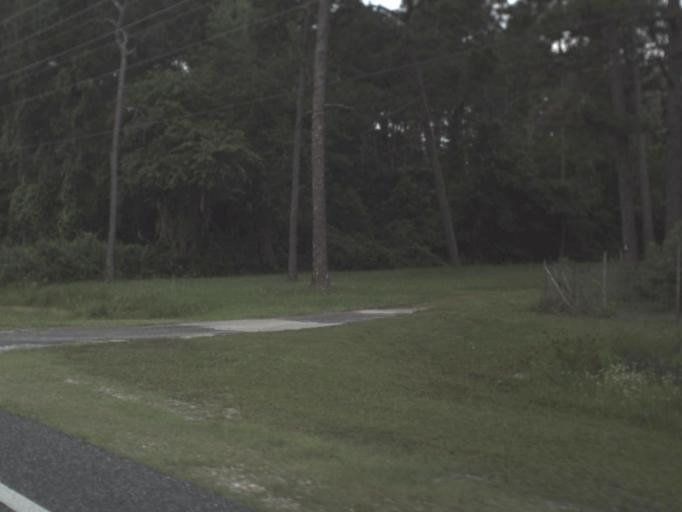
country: US
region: Florida
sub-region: Putnam County
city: Palatka
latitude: 29.7361
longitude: -81.6467
